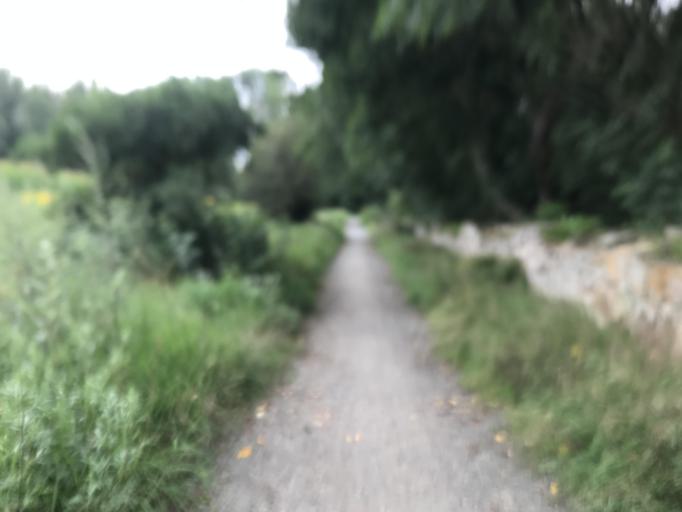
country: DE
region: Saxony-Anhalt
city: Weddersleben
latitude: 51.7743
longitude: 11.1157
